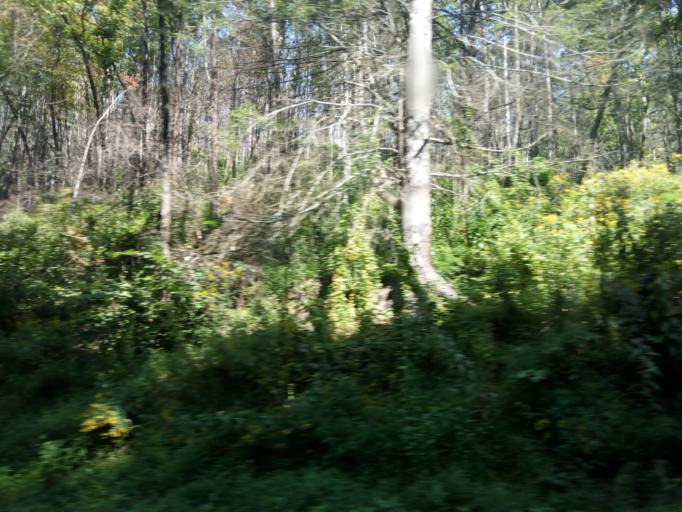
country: US
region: Tennessee
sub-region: Sevier County
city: Gatlinburg
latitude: 35.7284
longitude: -83.5011
